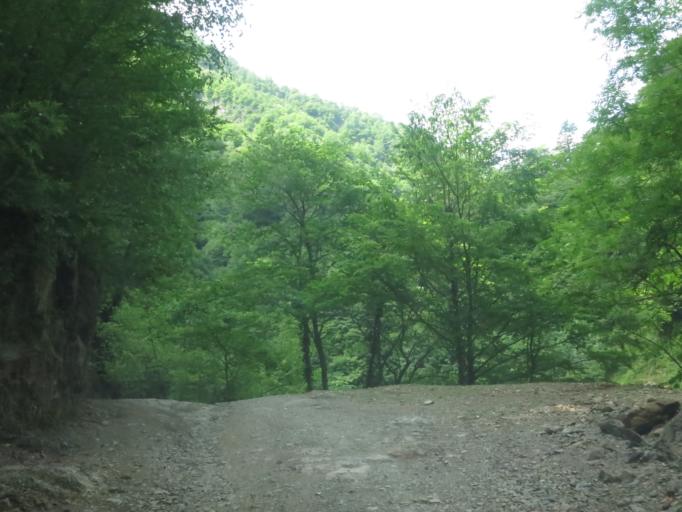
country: GE
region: Kakheti
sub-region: Telavi
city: Telavi
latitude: 42.2135
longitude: 45.4752
